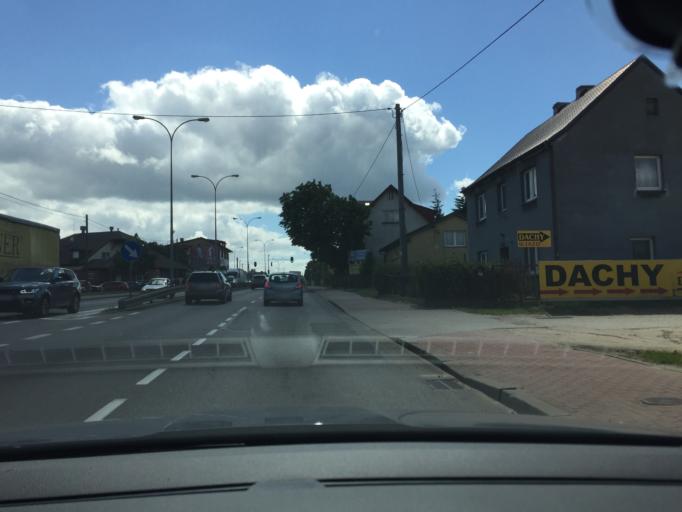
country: PL
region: Pomeranian Voivodeship
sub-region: Powiat wejherowski
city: Reda
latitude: 54.6034
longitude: 18.3490
